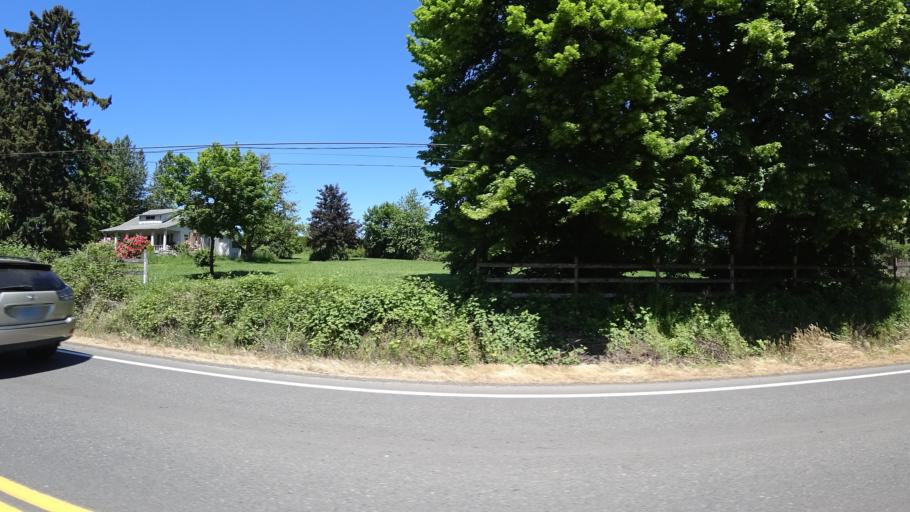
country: US
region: Oregon
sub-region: Clackamas County
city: Happy Valley
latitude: 45.4688
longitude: -122.4886
